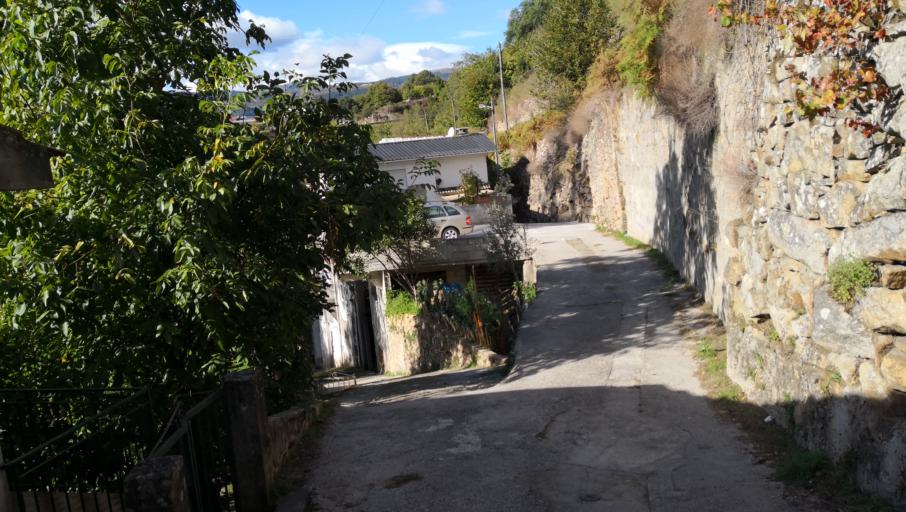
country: PT
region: Vila Real
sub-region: Vila Real
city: Vila Real
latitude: 41.2940
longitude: -7.7484
